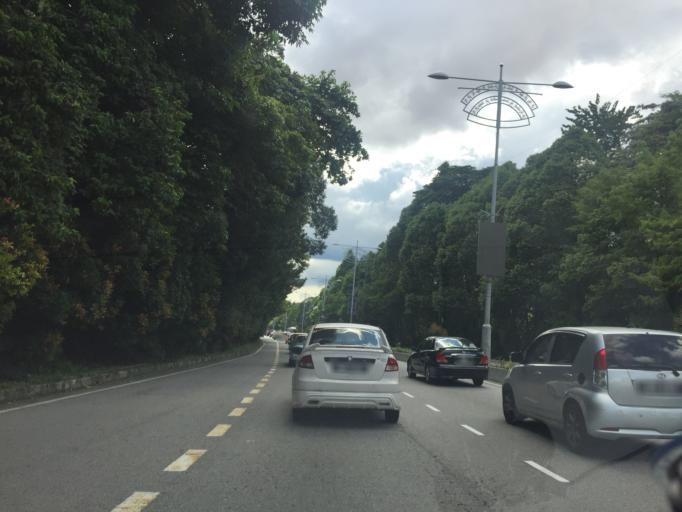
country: MY
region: Negeri Sembilan
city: Seremban
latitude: 2.7224
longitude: 101.9236
